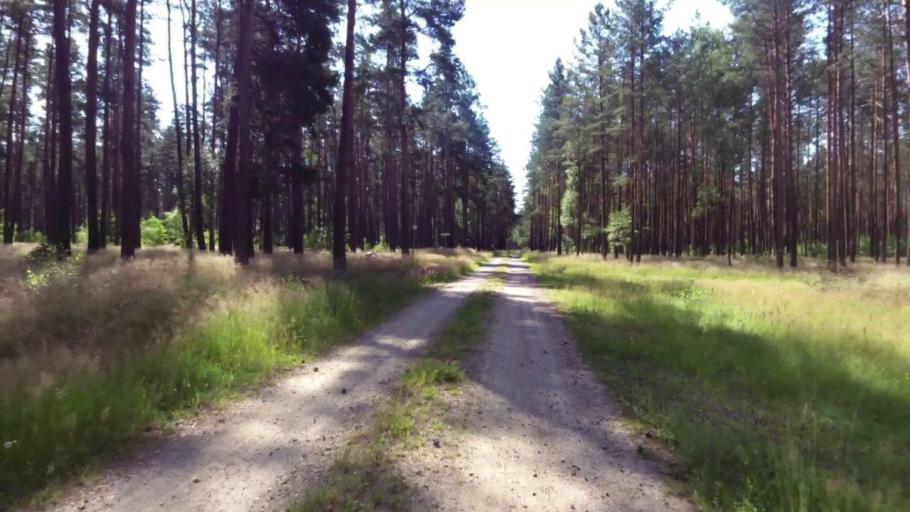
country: PL
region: West Pomeranian Voivodeship
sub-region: Powiat swidwinski
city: Polczyn-Zdroj
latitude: 53.8647
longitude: 16.1245
